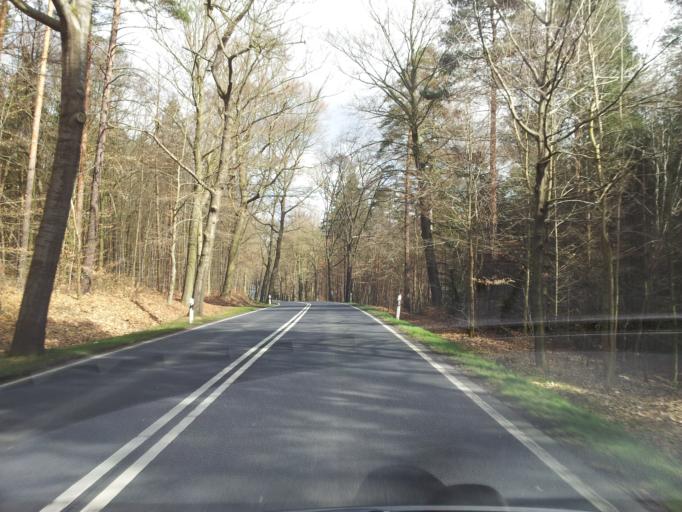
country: DE
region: Saxony
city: Ottendorf-Okrilla
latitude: 51.2237
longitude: 13.8436
